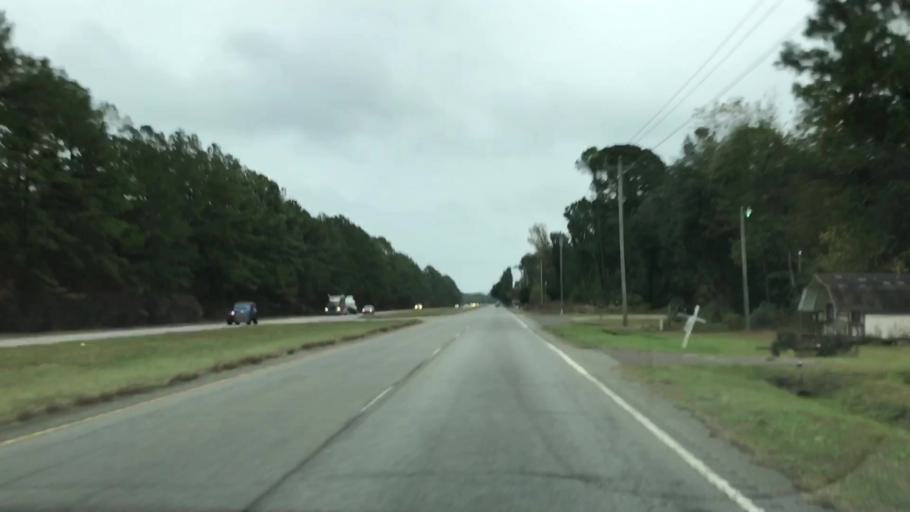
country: US
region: South Carolina
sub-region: Charleston County
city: Awendaw
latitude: 33.0381
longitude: -79.6073
